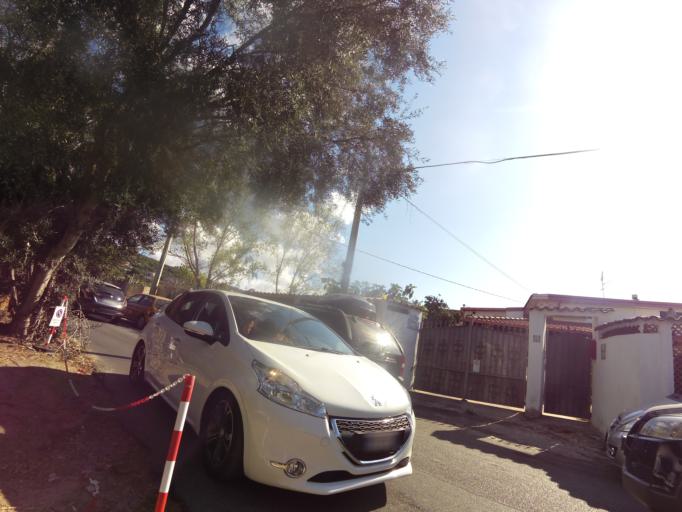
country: IT
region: Calabria
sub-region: Provincia di Vibo-Valentia
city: Santa Domenica
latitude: 38.6686
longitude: 15.8724
